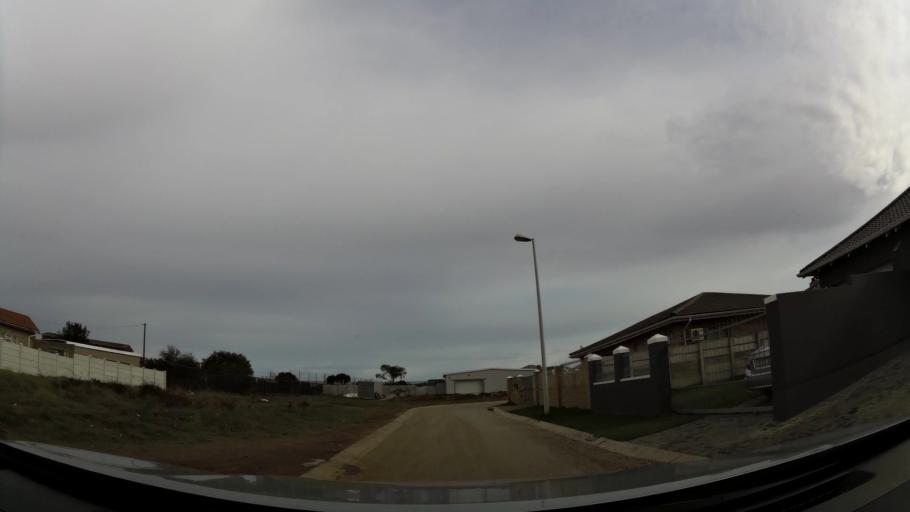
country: ZA
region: Eastern Cape
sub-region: Nelson Mandela Bay Metropolitan Municipality
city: Port Elizabeth
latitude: -33.9332
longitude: 25.5040
